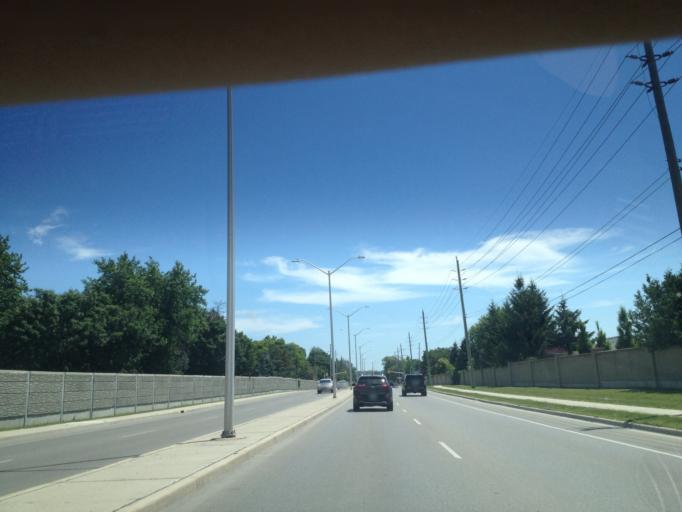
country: CA
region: Ontario
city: London
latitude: 42.9851
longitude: -81.3252
